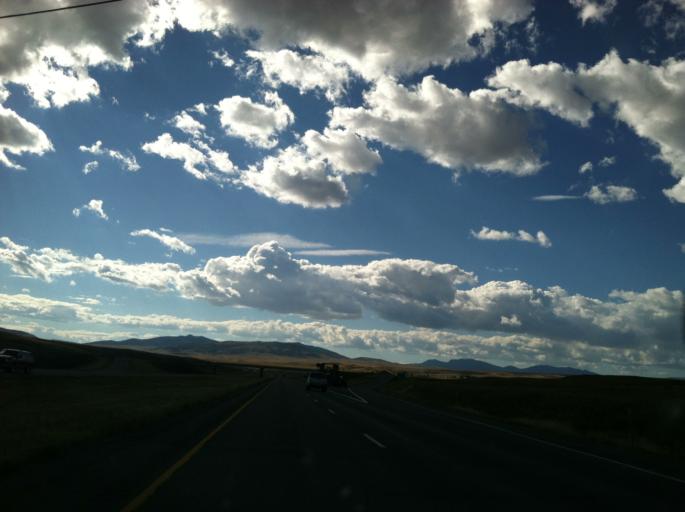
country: US
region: Montana
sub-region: Gallatin County
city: Three Forks
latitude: 45.9149
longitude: -111.7348
